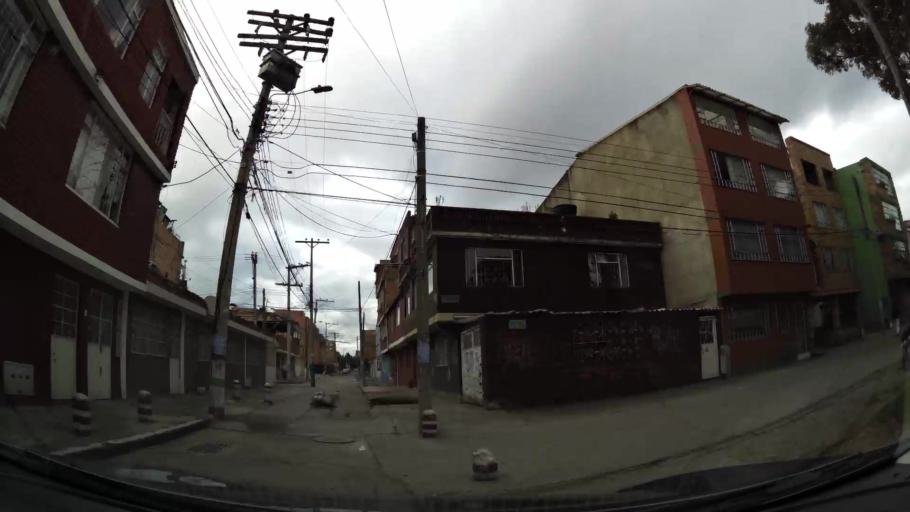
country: CO
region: Bogota D.C.
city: Barrio San Luis
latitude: 4.6991
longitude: -74.1086
